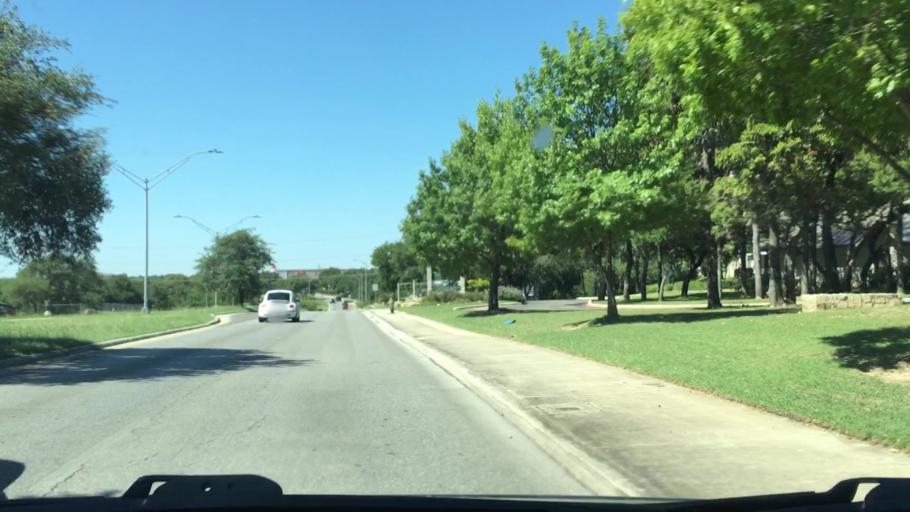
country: US
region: Texas
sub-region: Bexar County
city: Shavano Park
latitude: 29.5835
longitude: -98.5366
